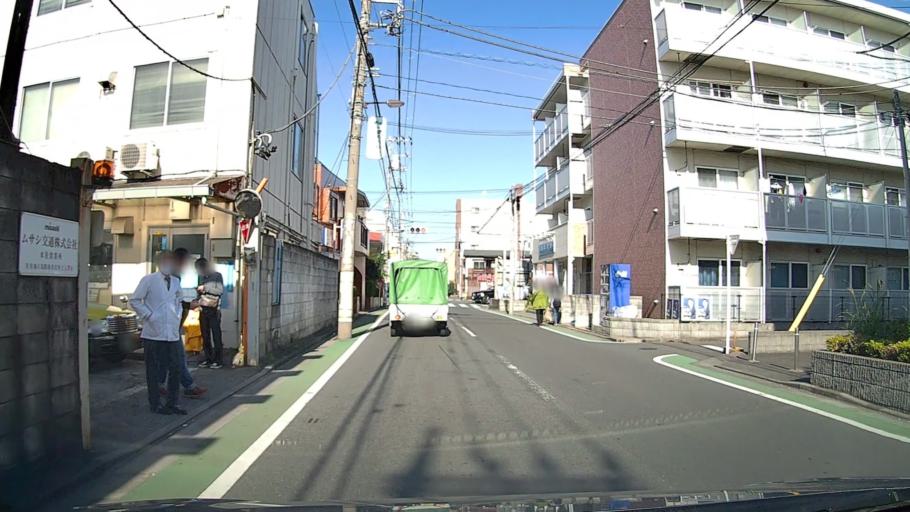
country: JP
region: Tokyo
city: Musashino
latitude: 35.7309
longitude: 139.5774
